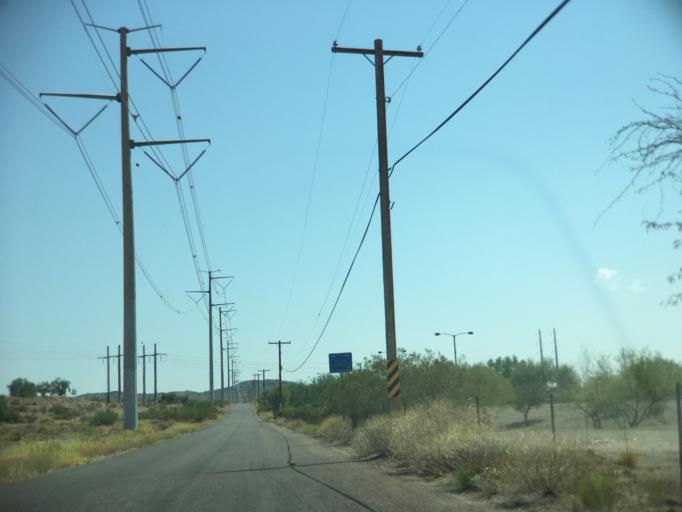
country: US
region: Arizona
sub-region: Maricopa County
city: Laveen
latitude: 33.3241
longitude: -112.1679
